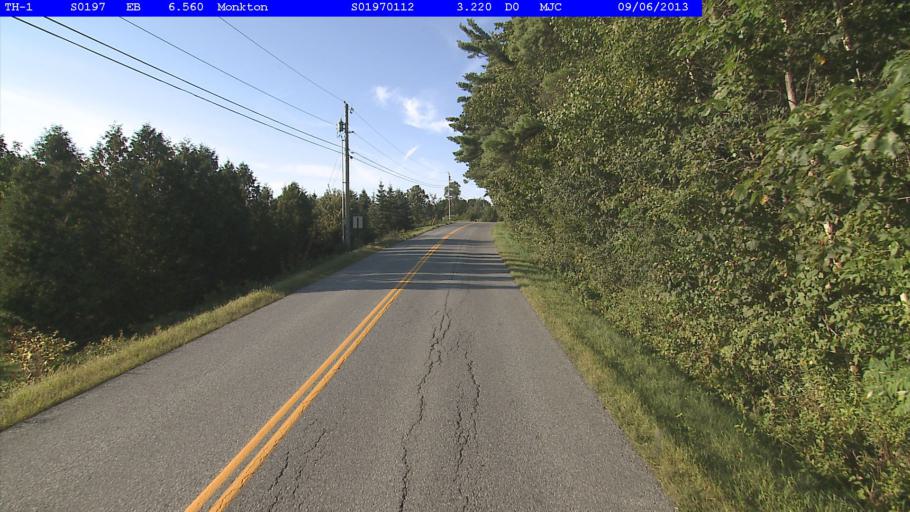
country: US
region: Vermont
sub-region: Chittenden County
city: Hinesburg
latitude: 44.2236
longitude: -73.1533
